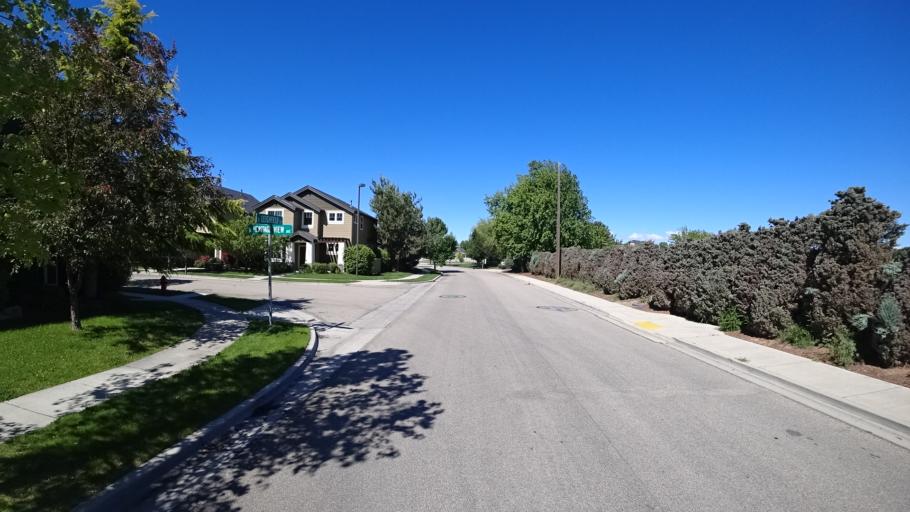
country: US
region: Idaho
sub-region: Ada County
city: Meridian
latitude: 43.6410
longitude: -116.3772
